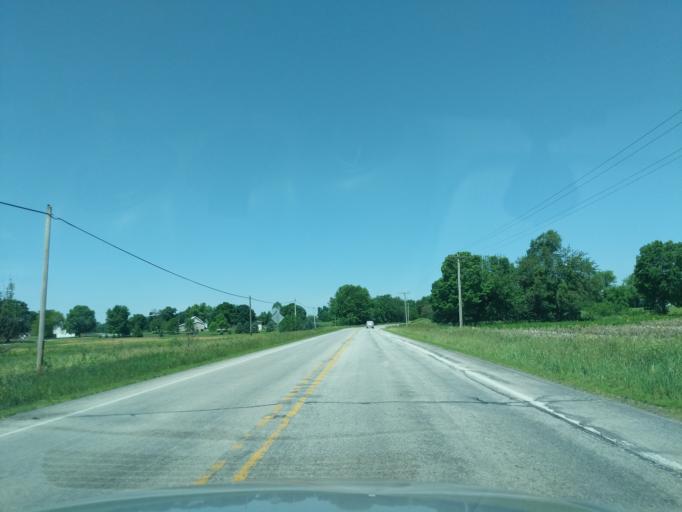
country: US
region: Indiana
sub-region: Whitley County
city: Columbia City
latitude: 41.1194
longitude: -85.4766
